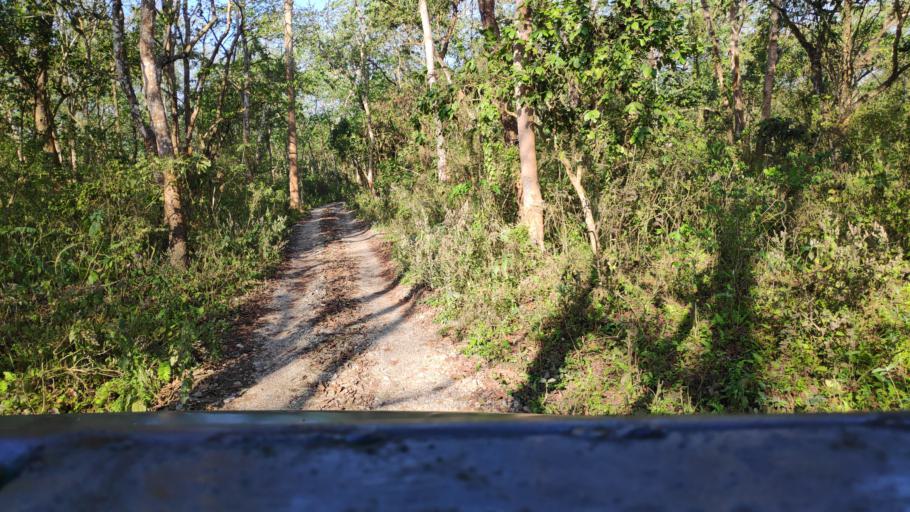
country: NP
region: Central Region
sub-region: Narayani Zone
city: Bharatpur
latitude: 27.5585
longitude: 84.5482
